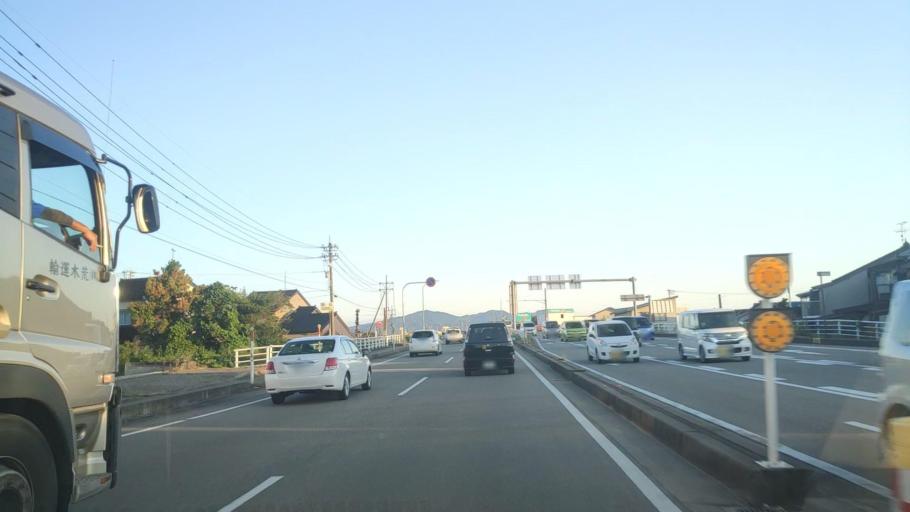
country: JP
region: Toyama
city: Himi
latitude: 36.8450
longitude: 136.9816
